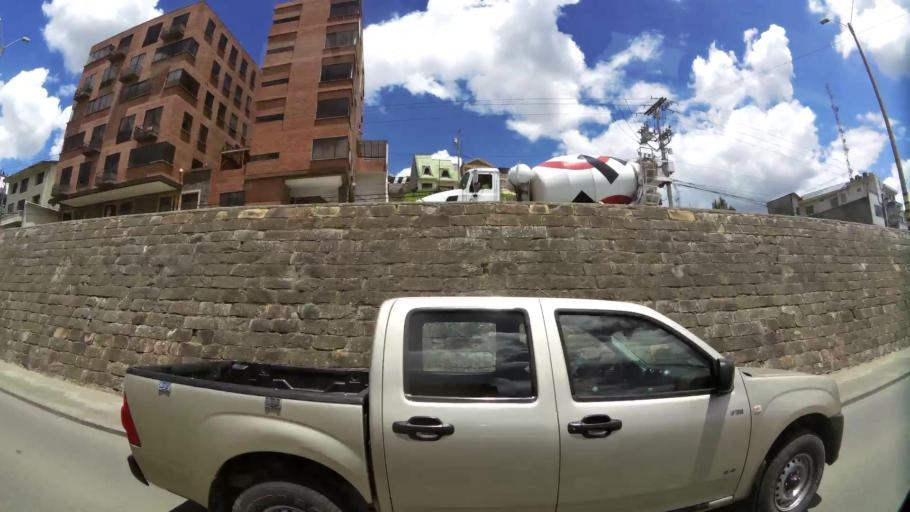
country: EC
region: Azuay
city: Cuenca
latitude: -2.8891
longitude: -79.0131
